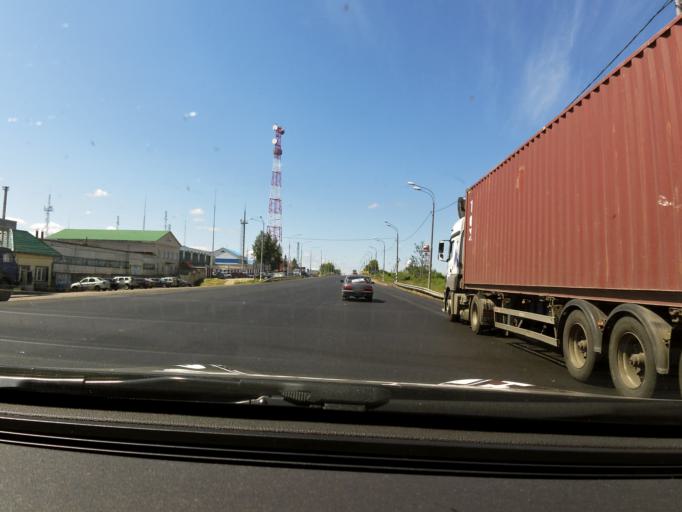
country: RU
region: Novgorod
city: Valday
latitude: 57.9522
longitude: 33.2855
